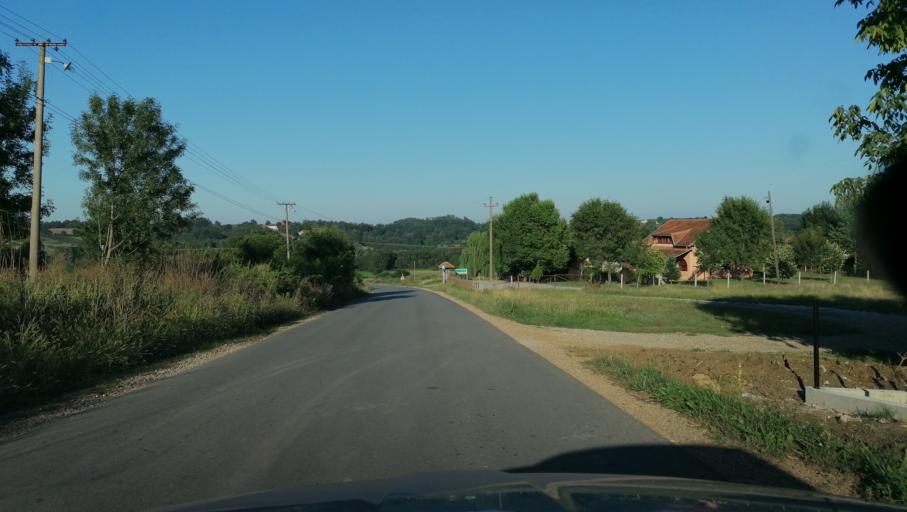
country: RS
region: Central Serbia
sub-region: Sumadijski Okrug
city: Kragujevac
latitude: 44.1072
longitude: 20.8245
